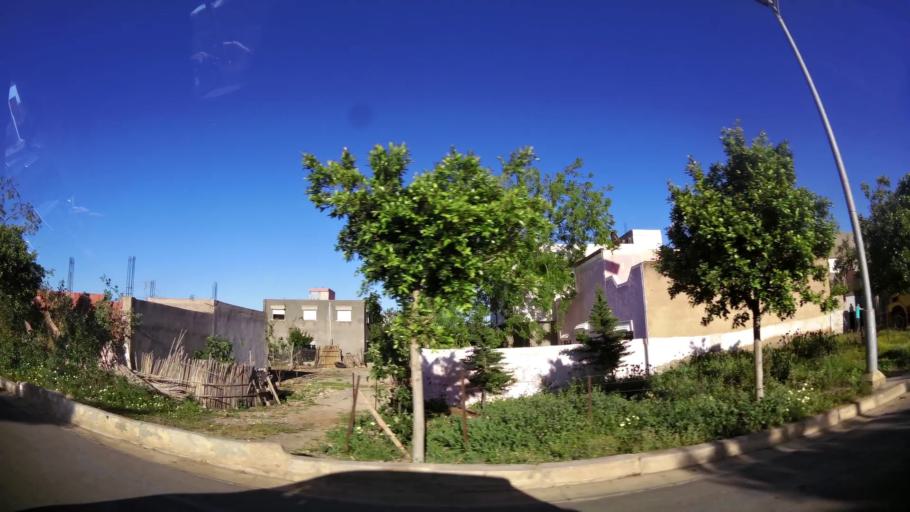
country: MA
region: Oriental
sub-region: Berkane-Taourirt
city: Madagh
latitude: 35.0798
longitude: -2.2444
